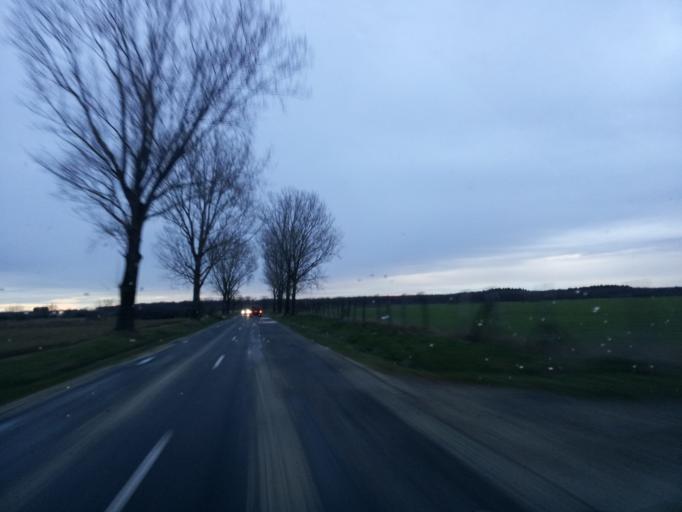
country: HU
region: Gyor-Moson-Sopron
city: Fertoszentmiklos
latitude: 47.5109
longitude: 16.7946
